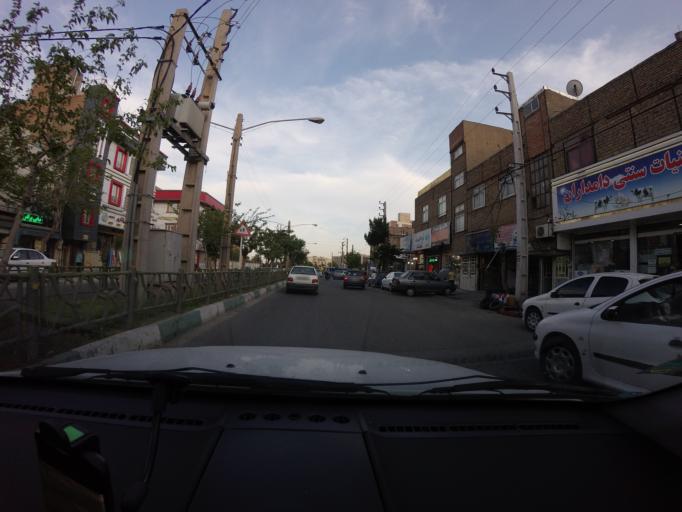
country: IR
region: Tehran
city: Eslamshahr
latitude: 35.5271
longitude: 51.2278
